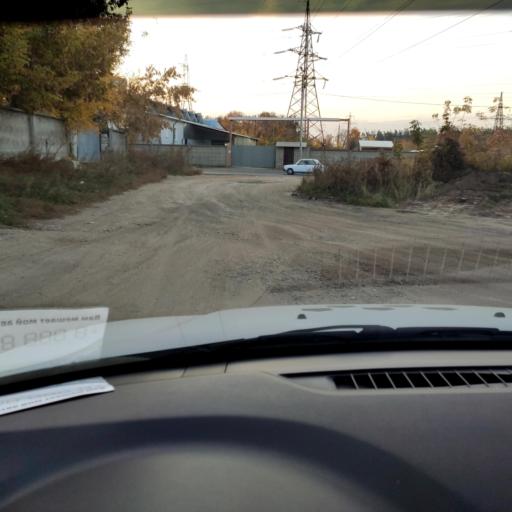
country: RU
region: Samara
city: Zhigulevsk
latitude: 53.5166
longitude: 49.4751
